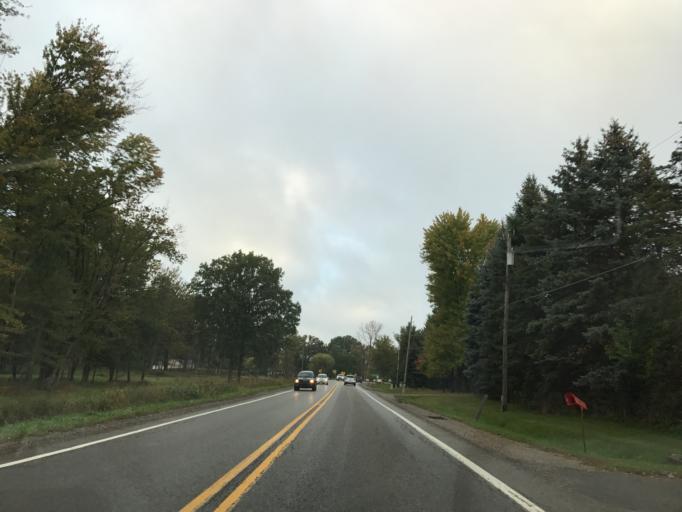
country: US
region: Michigan
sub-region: Oakland County
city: South Lyon
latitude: 42.4880
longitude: -83.6132
